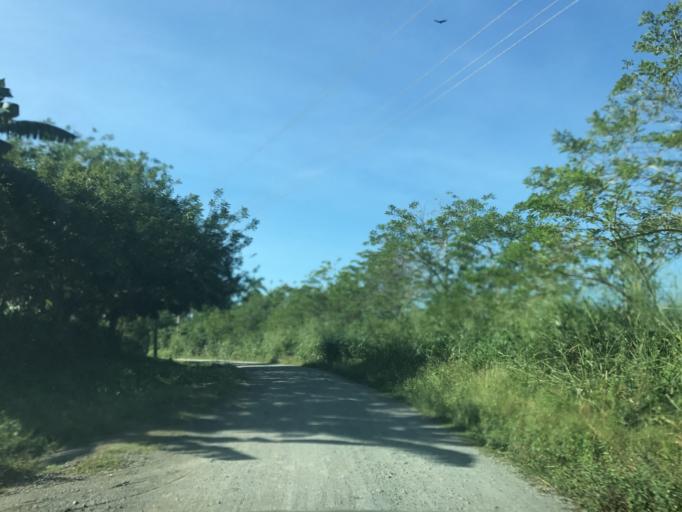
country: CU
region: Camaguey
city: Florida
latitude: 21.4817
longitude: -78.1777
